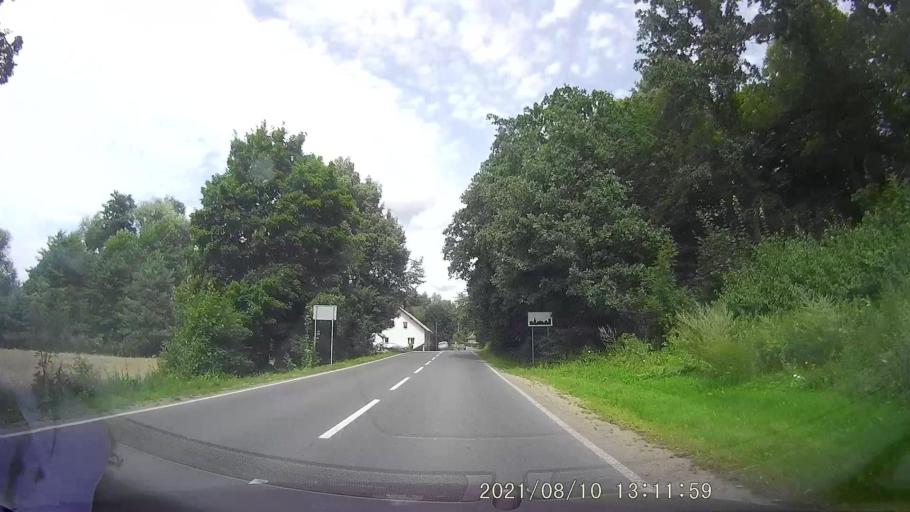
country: PL
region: Lower Silesian Voivodeship
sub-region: Powiat klodzki
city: Bozkow
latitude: 50.5120
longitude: 16.5140
